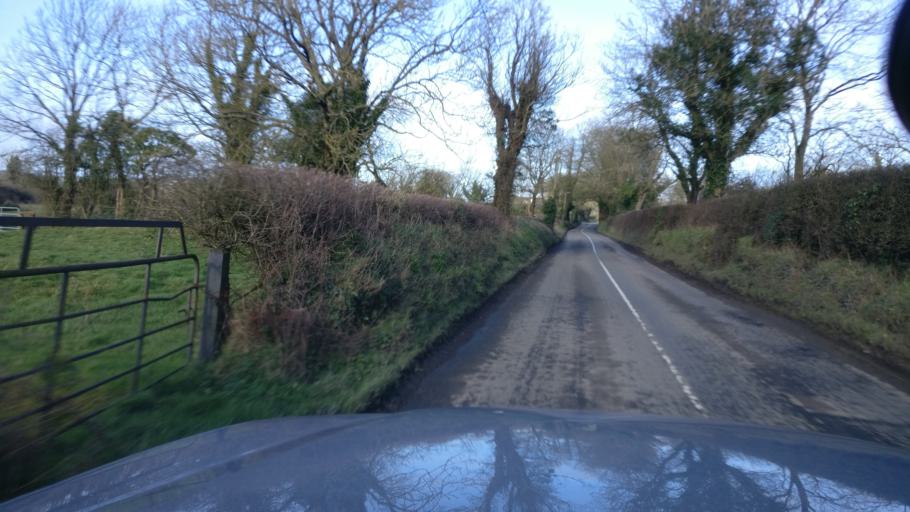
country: IE
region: Leinster
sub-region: Kilkenny
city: Castlecomer
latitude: 52.8839
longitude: -7.1622
